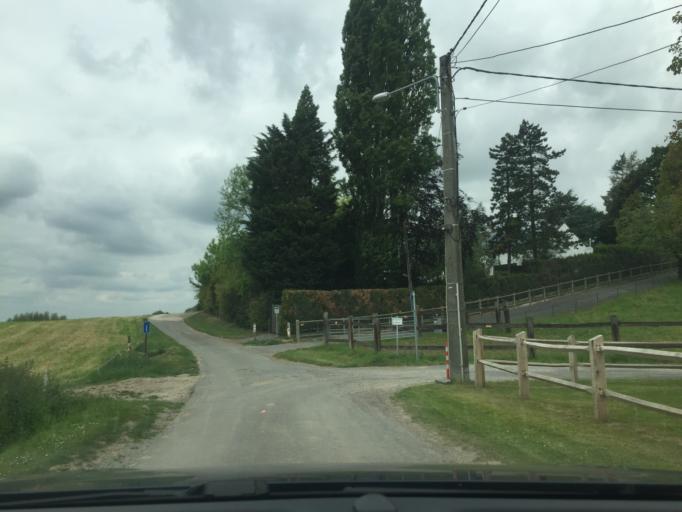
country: BE
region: Wallonia
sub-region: Province du Hainaut
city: Tournai
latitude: 50.6551
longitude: 3.3880
